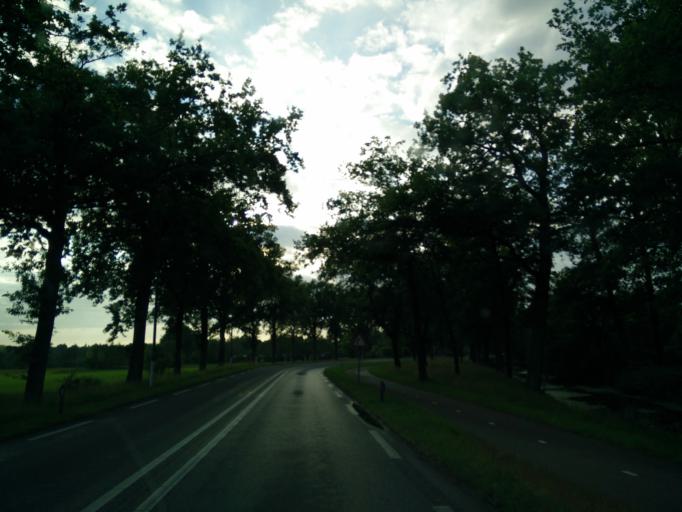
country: NL
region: Utrecht
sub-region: Gemeente Woudenberg
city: Woudenberg
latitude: 52.1000
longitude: 5.4150
